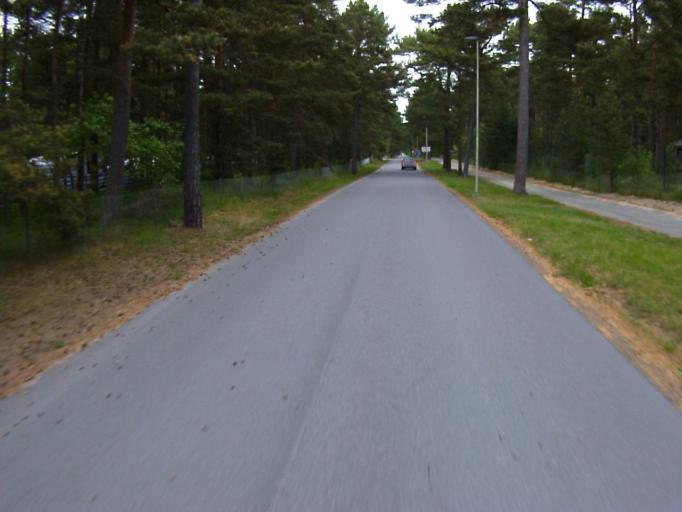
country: SE
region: Skane
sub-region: Kristianstads Kommun
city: Ahus
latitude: 55.9405
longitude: 14.3174
